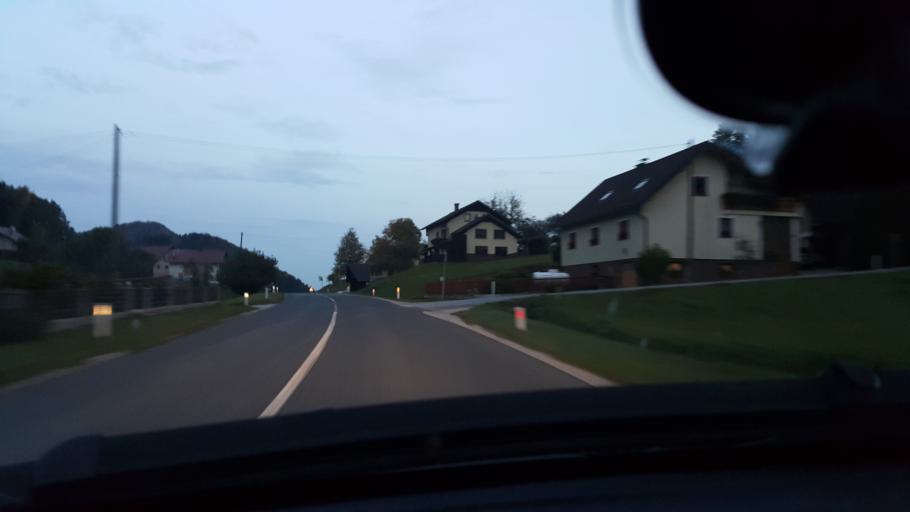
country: SI
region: Vitanje
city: Vitanje
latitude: 46.3773
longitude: 15.3331
